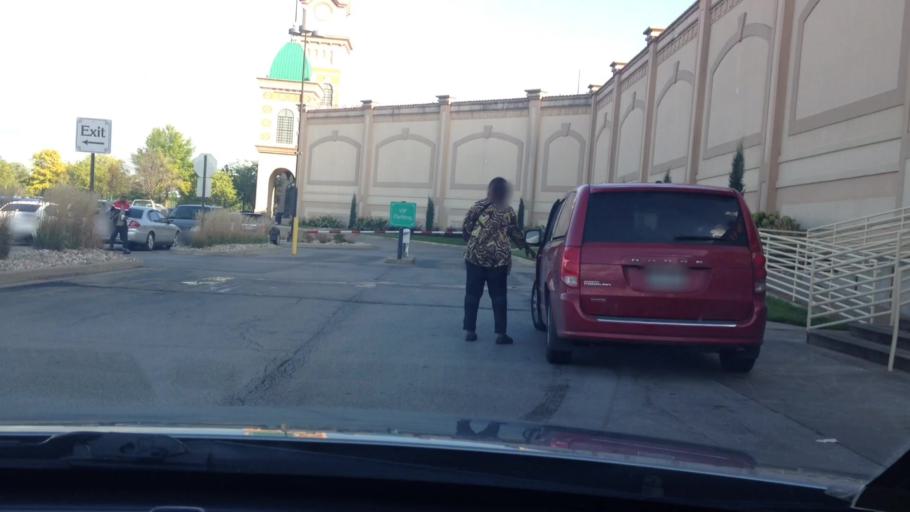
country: US
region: Missouri
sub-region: Clay County
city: Claycomo
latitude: 39.1509
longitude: -94.4845
